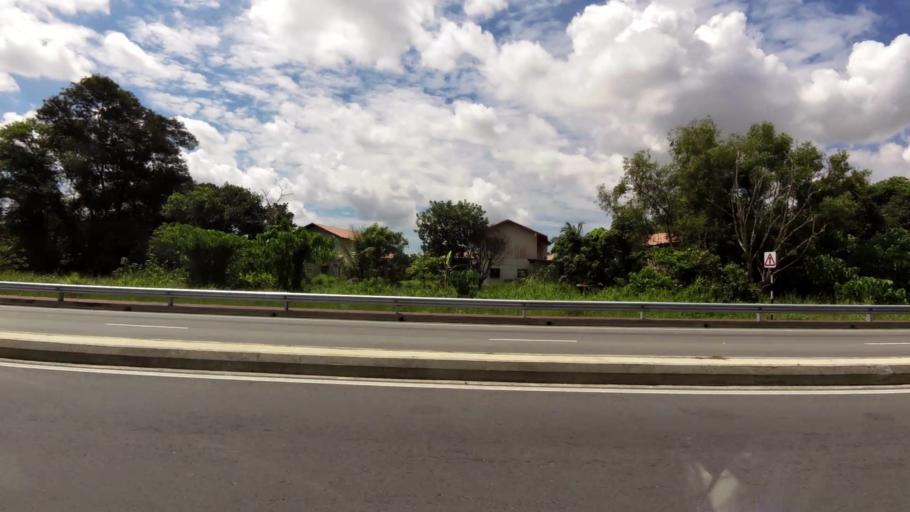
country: BN
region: Brunei and Muara
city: Bandar Seri Begawan
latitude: 4.9398
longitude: 114.9043
